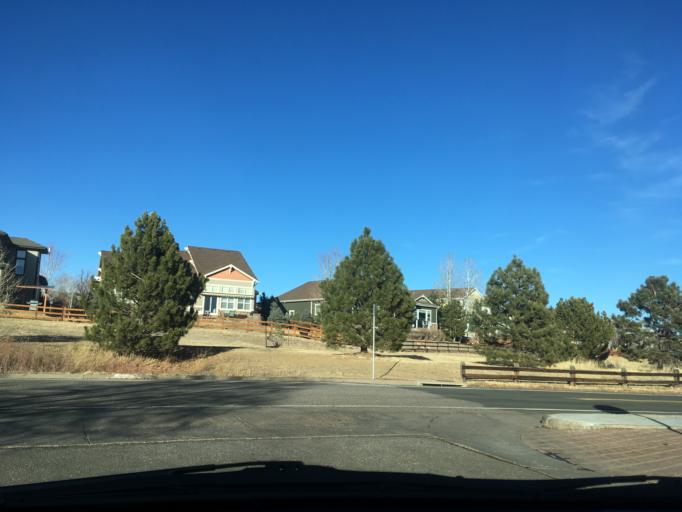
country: US
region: Colorado
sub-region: Broomfield County
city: Broomfield
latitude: 39.9357
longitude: -105.0440
